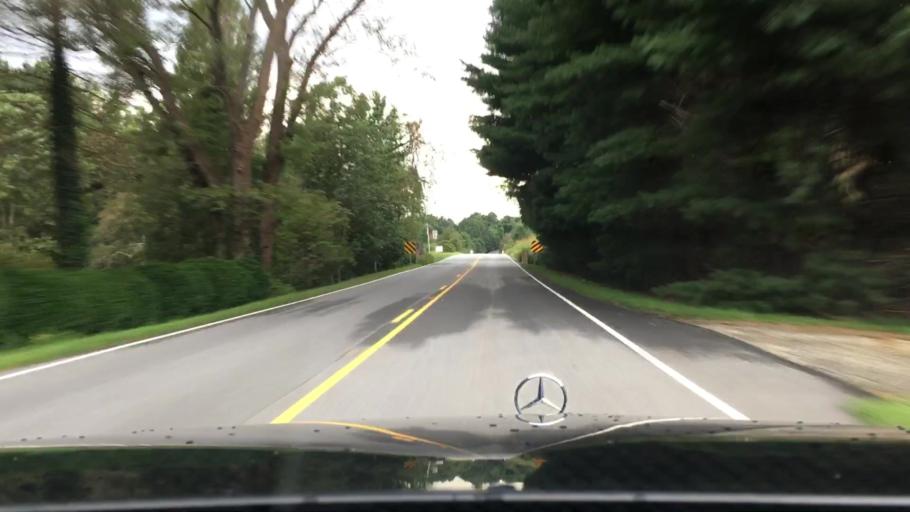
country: US
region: Virginia
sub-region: Nelson County
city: Lovingston
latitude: 37.7997
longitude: -78.9587
